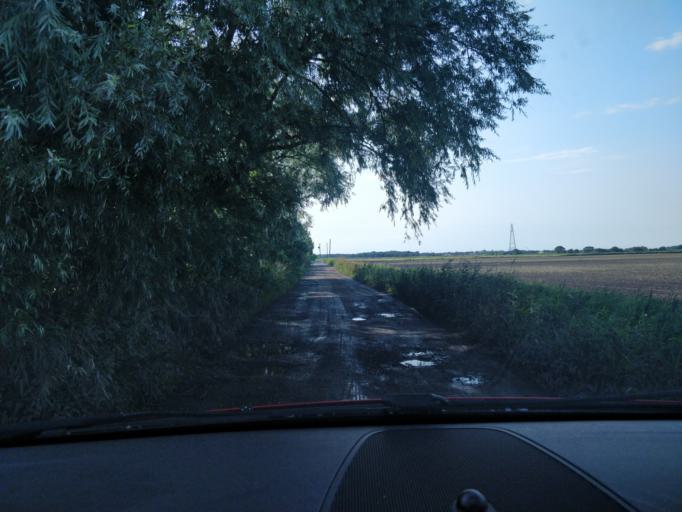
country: GB
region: England
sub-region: Lancashire
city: Banks
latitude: 53.6539
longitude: -2.9211
